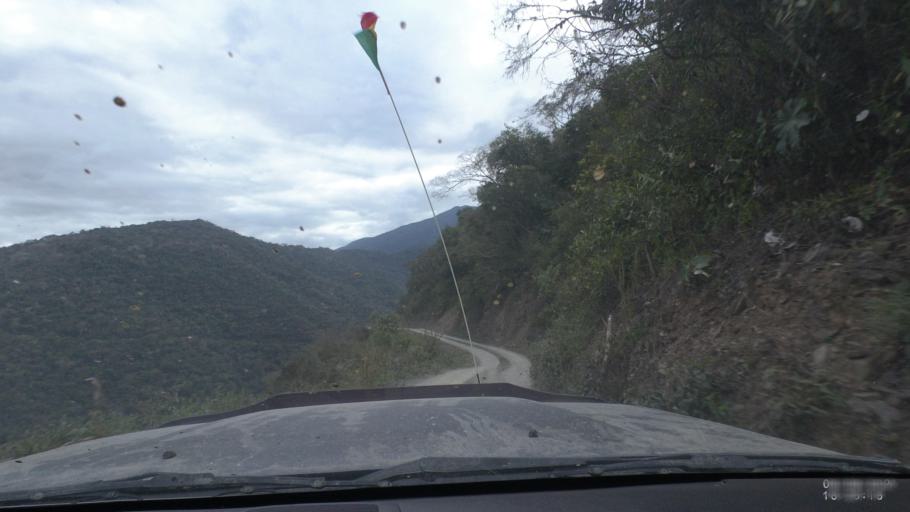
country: BO
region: La Paz
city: Quime
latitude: -16.5354
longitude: -66.7600
